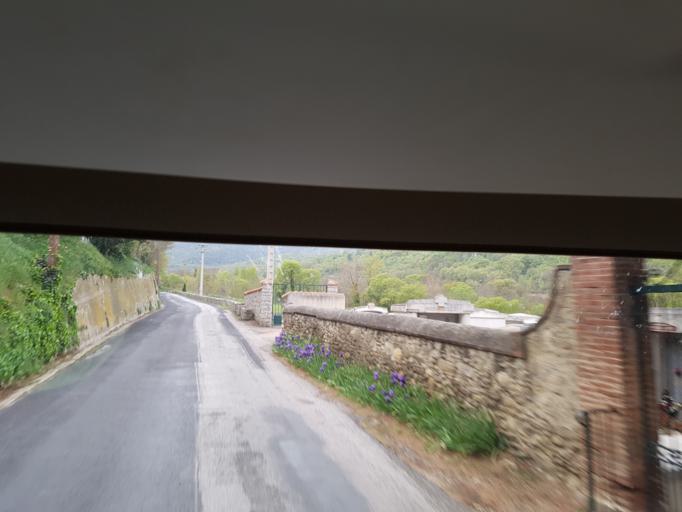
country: FR
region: Languedoc-Roussillon
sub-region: Departement des Pyrenees-Orientales
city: Prades
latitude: 42.6069
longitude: 2.4174
